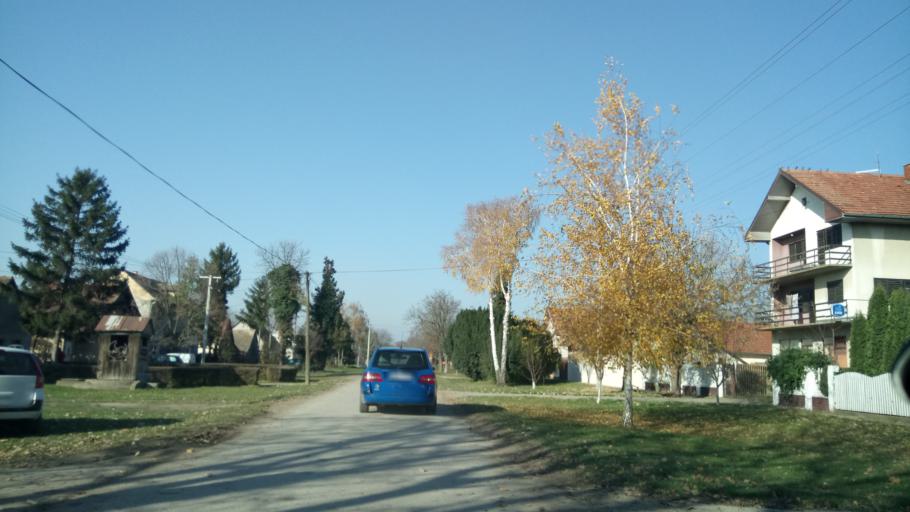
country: RS
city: Ljukovo
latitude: 45.0534
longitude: 20.0260
